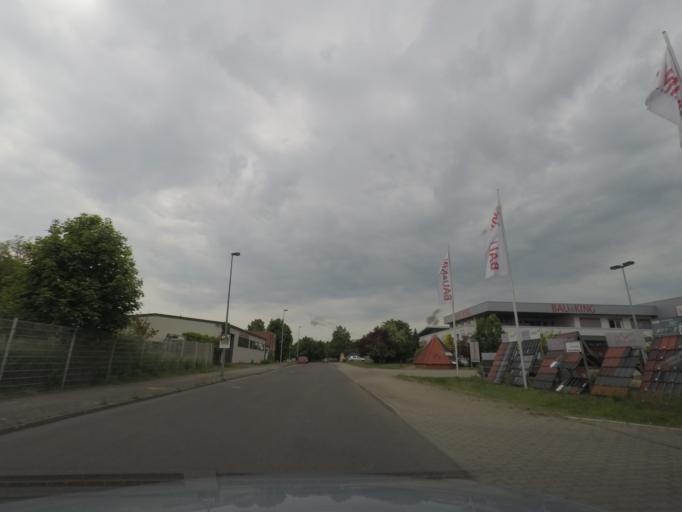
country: DE
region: Berlin
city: Mahlsdorf
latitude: 52.5132
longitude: 13.6385
